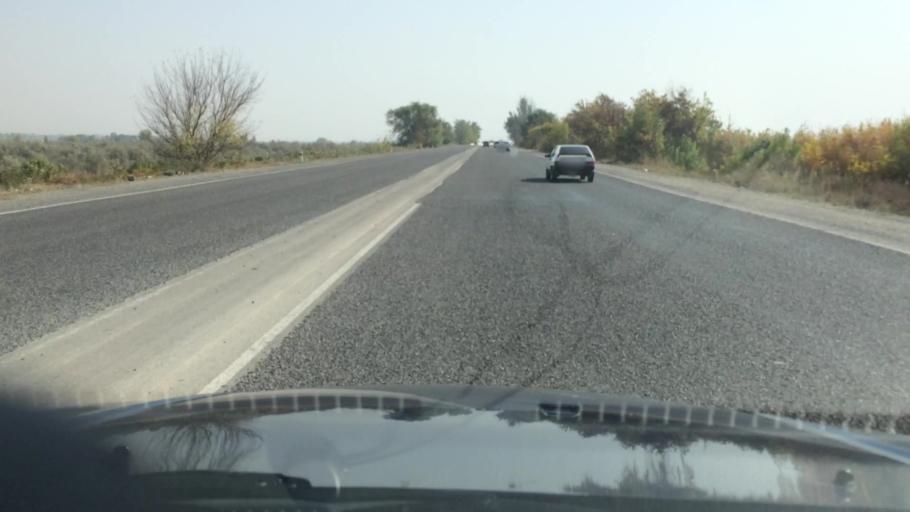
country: KG
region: Chuy
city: Kant
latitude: 42.9557
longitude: 74.9367
